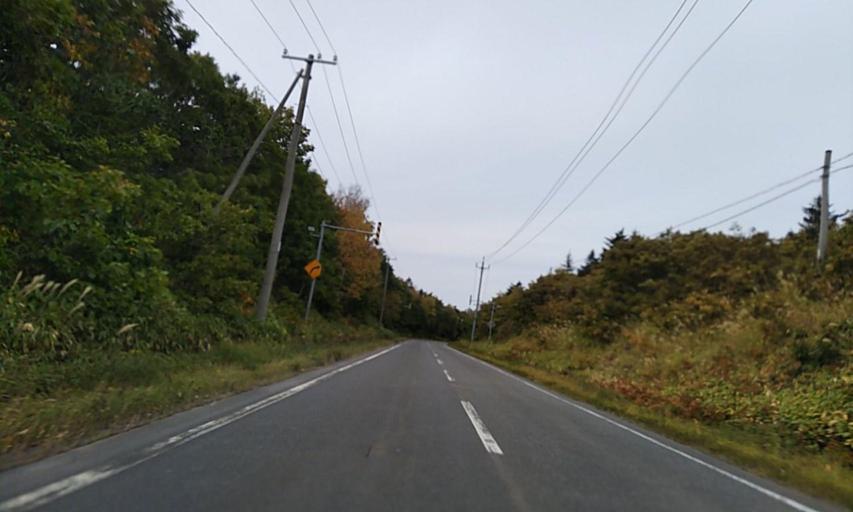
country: JP
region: Hokkaido
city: Makubetsu
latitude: 44.9988
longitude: 141.6964
